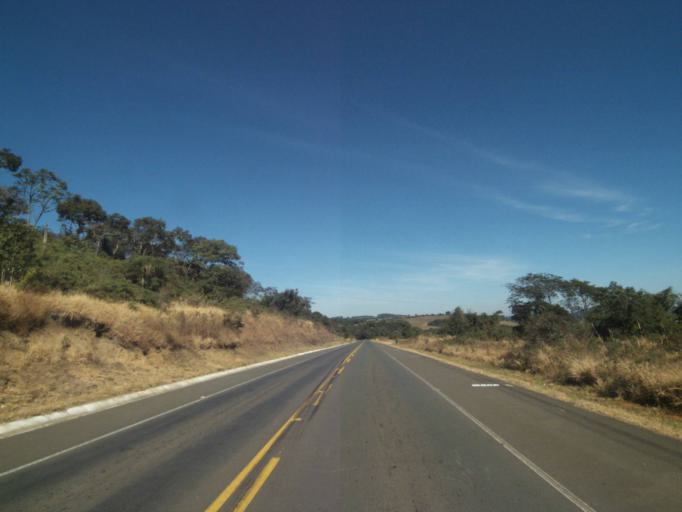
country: BR
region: Parana
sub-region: Tibagi
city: Tibagi
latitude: -24.7831
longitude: -50.4679
